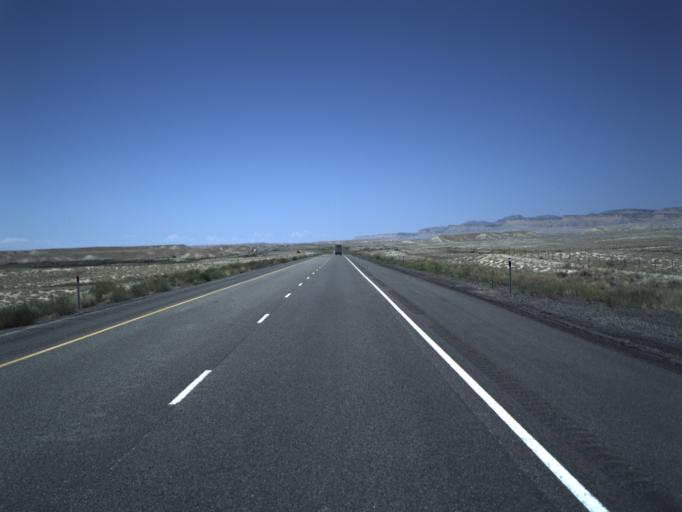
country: US
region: Utah
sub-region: Grand County
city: Moab
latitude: 38.9391
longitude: -109.4932
